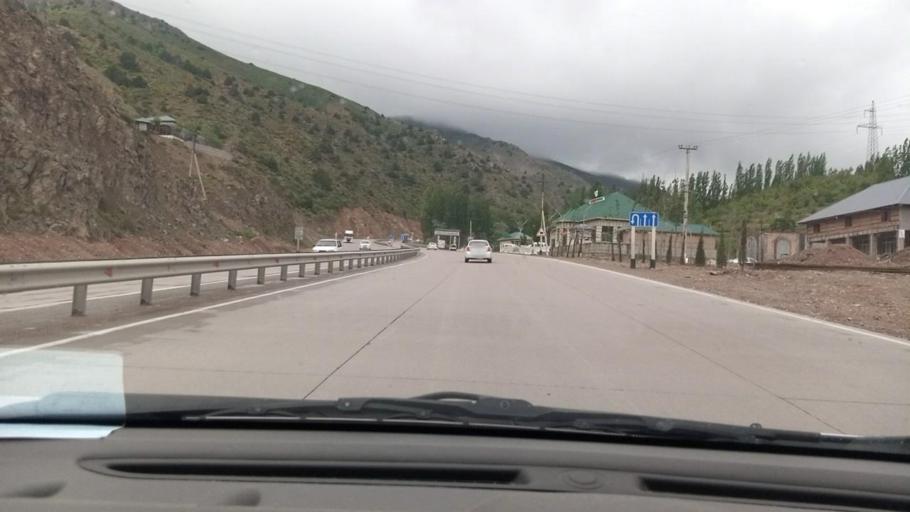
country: TJ
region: Viloyati Sughd
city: Shaydon
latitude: 41.0335
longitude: 70.5880
